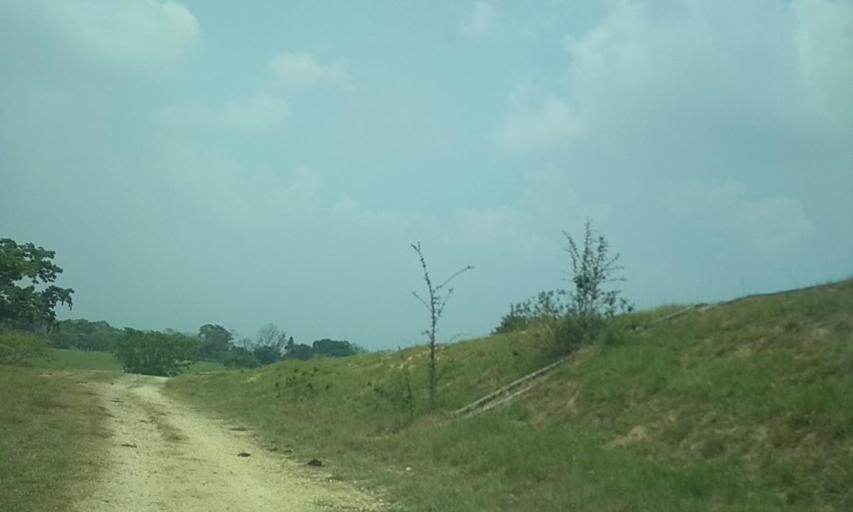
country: MX
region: Tabasco
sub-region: Huimanguillo
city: Francisco Rueda
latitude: 17.8021
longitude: -94.0614
